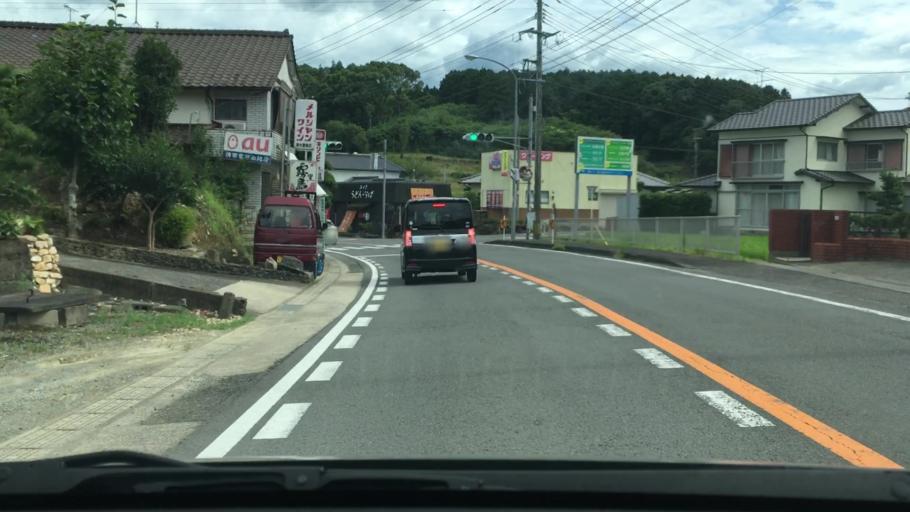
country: JP
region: Nagasaki
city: Togitsu
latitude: 32.9650
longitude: 129.7807
